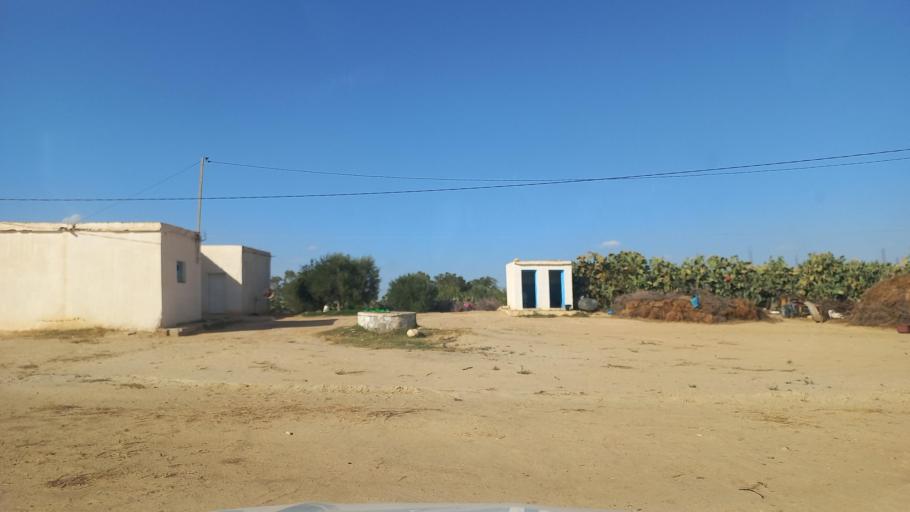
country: TN
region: Al Qasrayn
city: Kasserine
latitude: 35.2563
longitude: 9.0309
